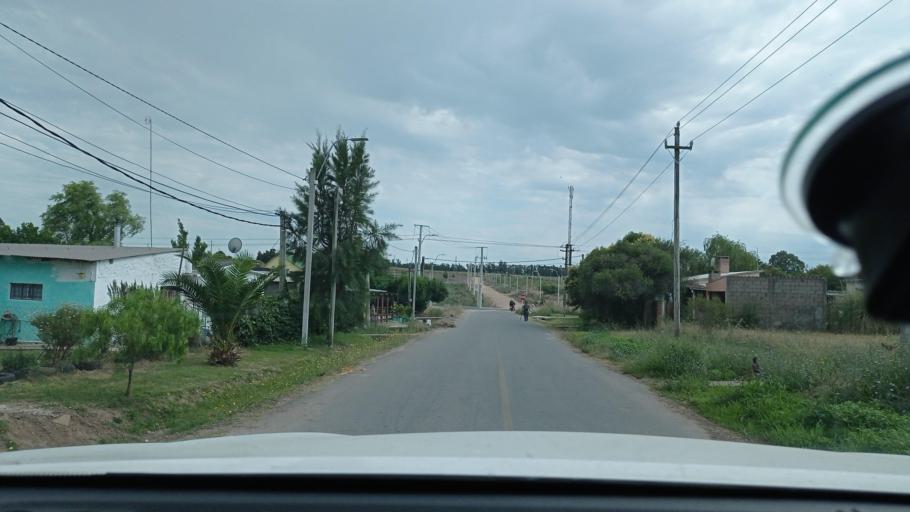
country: UY
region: Canelones
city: Pando
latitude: -34.7120
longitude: -55.9703
